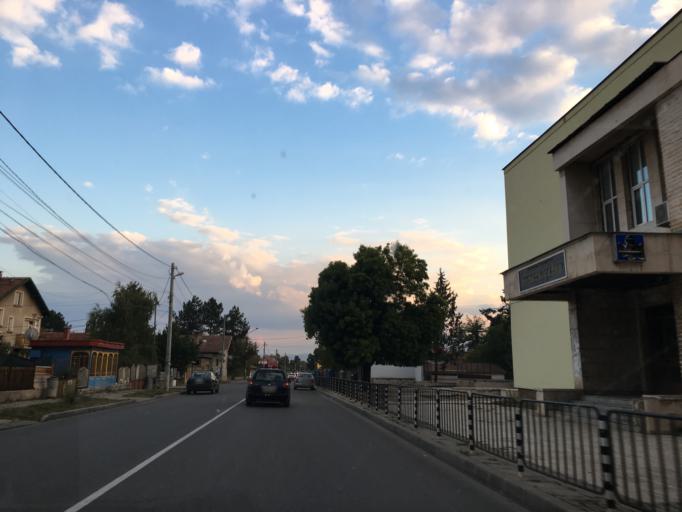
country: BG
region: Sofia-Capital
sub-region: Stolichna Obshtina
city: Sofia
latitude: 42.8252
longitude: 23.3539
